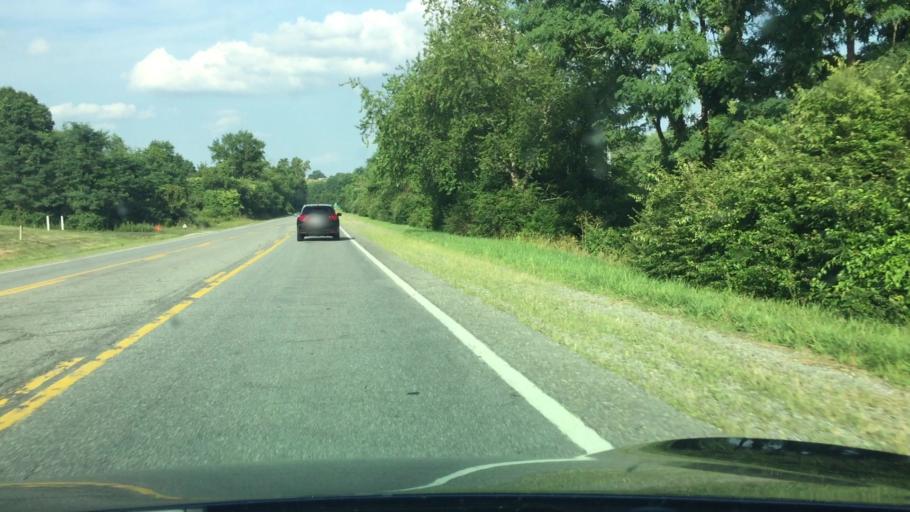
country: US
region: Virginia
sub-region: City of Radford
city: Radford
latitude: 37.1329
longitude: -80.6253
